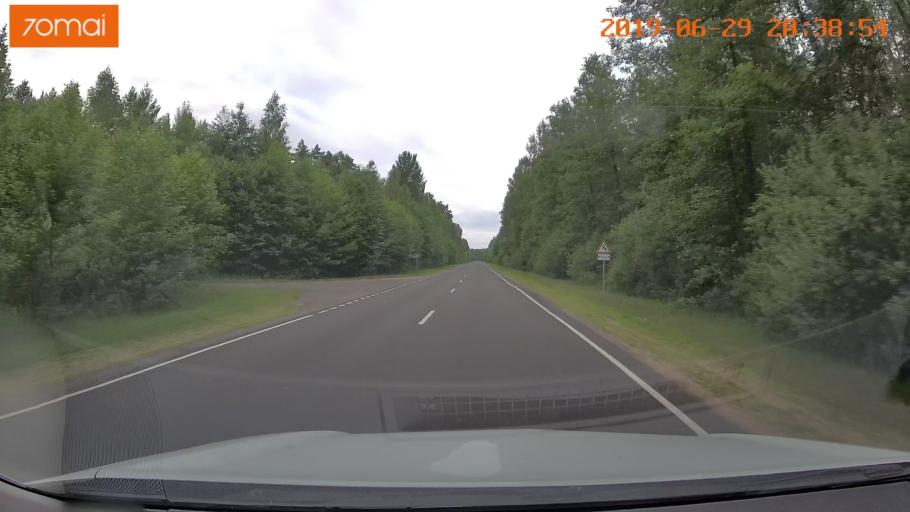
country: BY
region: Brest
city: Hantsavichy
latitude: 52.5557
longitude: 26.3638
